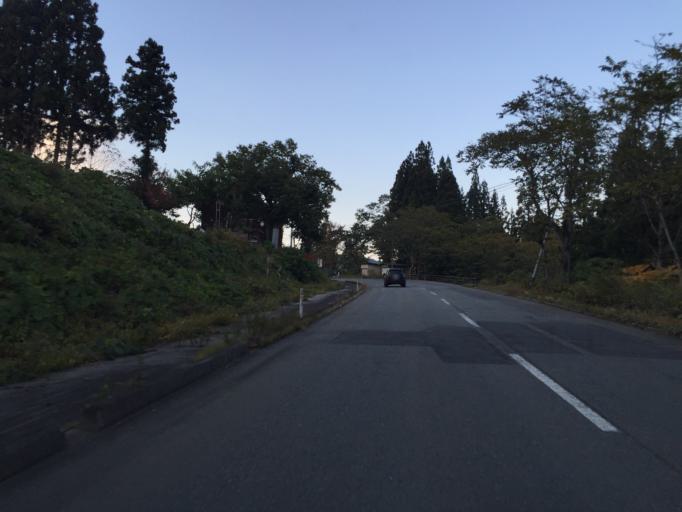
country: JP
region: Yamagata
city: Yonezawa
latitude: 37.8696
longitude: 139.9838
